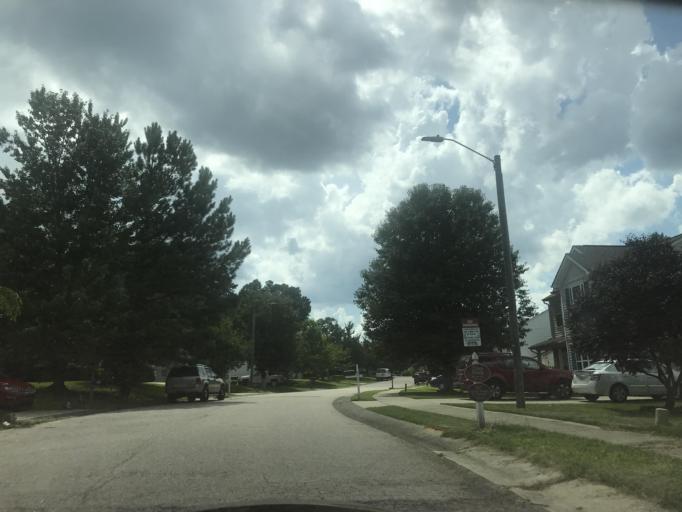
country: US
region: North Carolina
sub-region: Wake County
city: Knightdale
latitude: 35.8360
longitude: -78.5650
